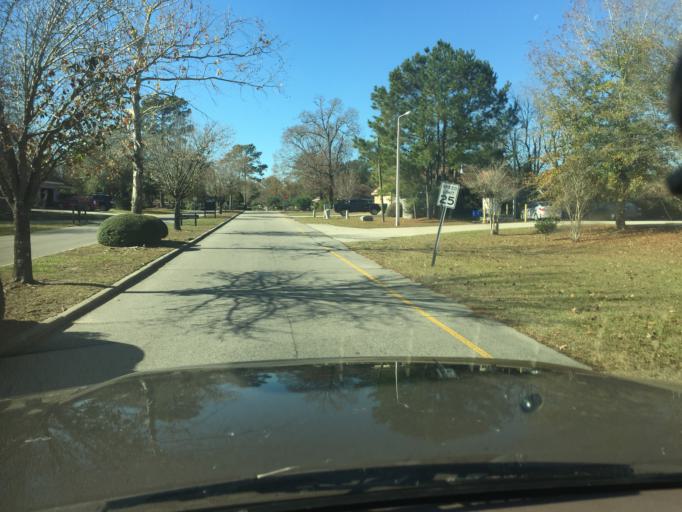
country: US
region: Louisiana
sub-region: Saint Tammany Parish
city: Slidell
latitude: 30.2976
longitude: -89.7222
